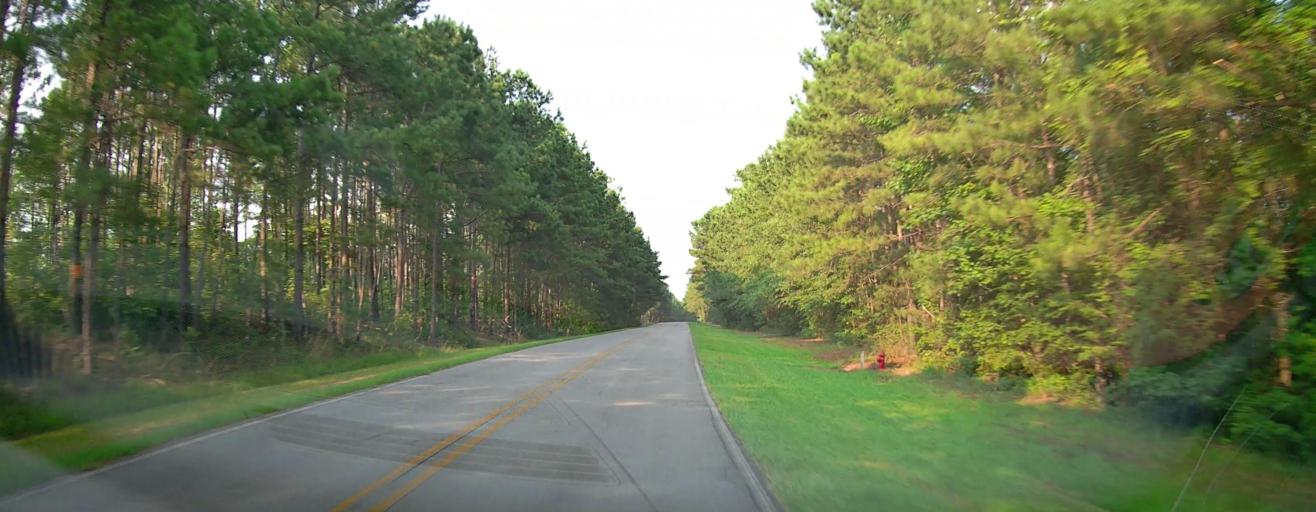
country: US
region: Georgia
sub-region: Monroe County
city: Forsyth
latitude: 32.9997
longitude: -83.7544
